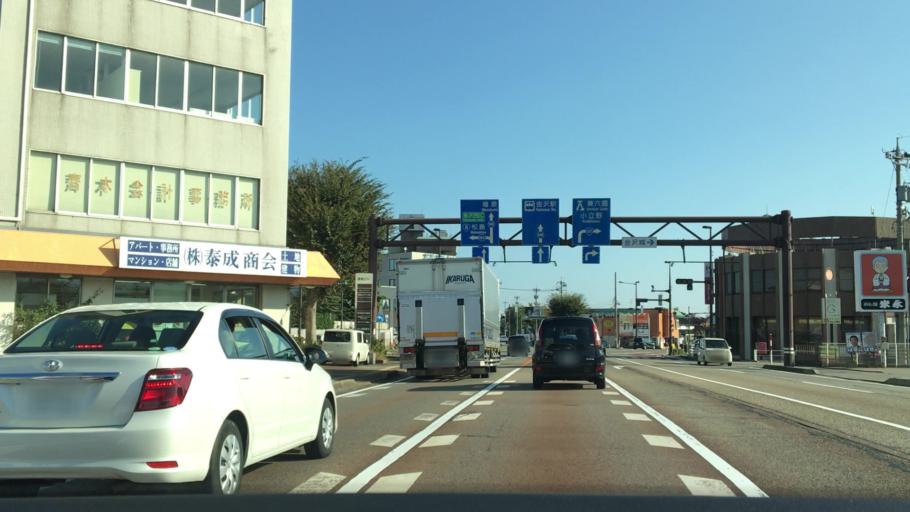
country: JP
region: Ishikawa
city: Nonoichi
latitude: 36.5435
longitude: 136.6270
